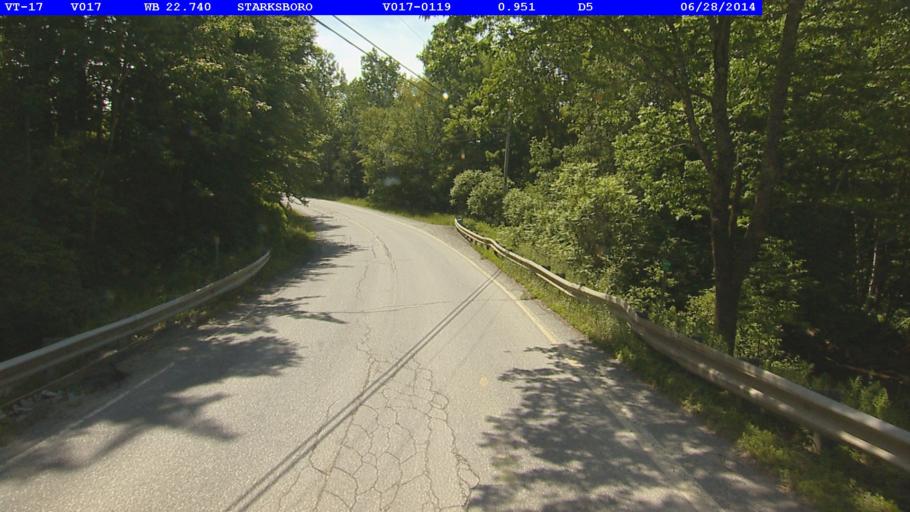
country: US
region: Vermont
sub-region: Addison County
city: Bristol
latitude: 44.1694
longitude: -73.0022
